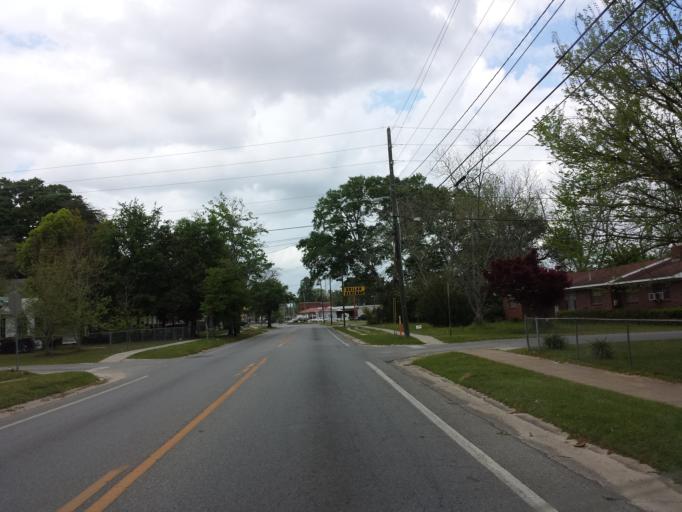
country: US
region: Georgia
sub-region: Cook County
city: Sparks
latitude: 31.1645
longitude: -83.4370
